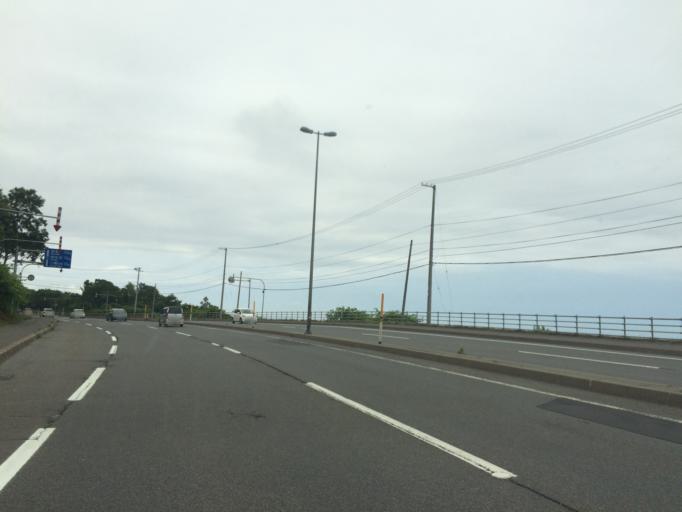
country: JP
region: Hokkaido
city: Otaru
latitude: 43.1613
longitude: 141.1079
